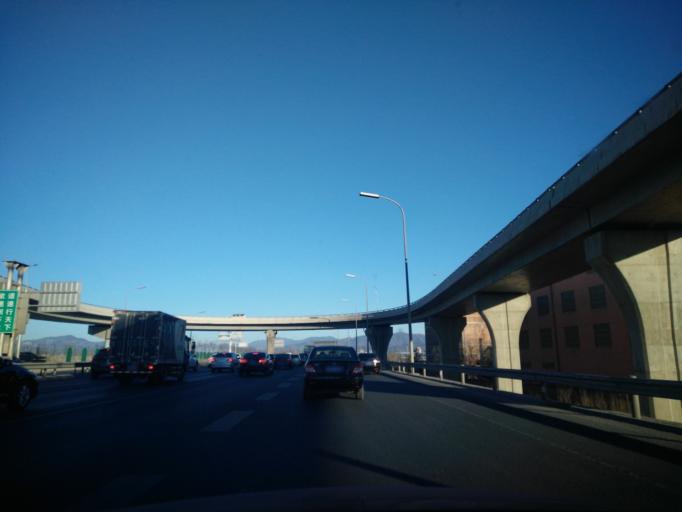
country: CN
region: Beijing
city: Lugu
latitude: 39.8673
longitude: 116.2060
